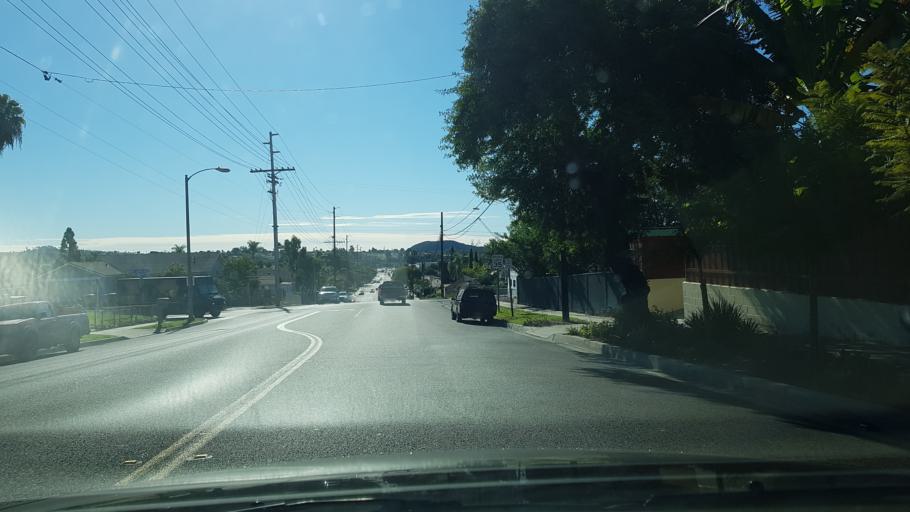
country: US
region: California
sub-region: San Diego County
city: Vista
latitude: 33.1972
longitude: -117.2795
